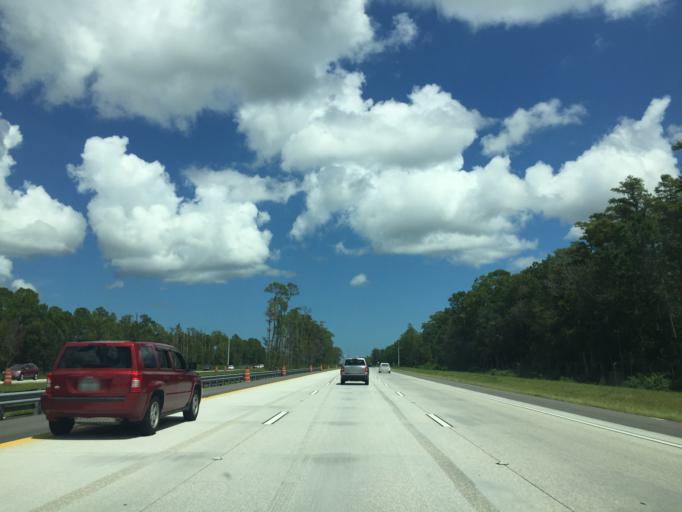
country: US
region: Florida
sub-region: Volusia County
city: Samsula-Spruce Creek
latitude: 29.0886
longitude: -81.1643
